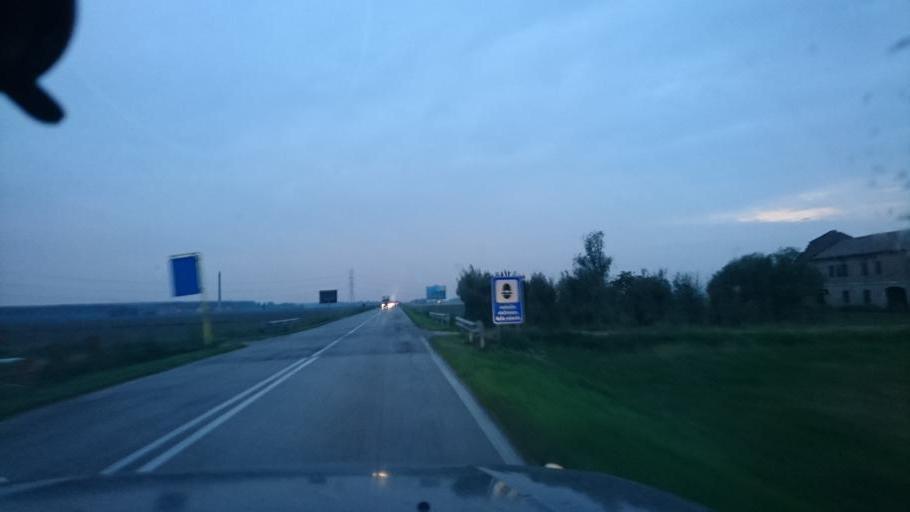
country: IT
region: Veneto
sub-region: Provincia di Rovigo
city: Porto Tolle
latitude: 44.9485
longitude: 12.2919
